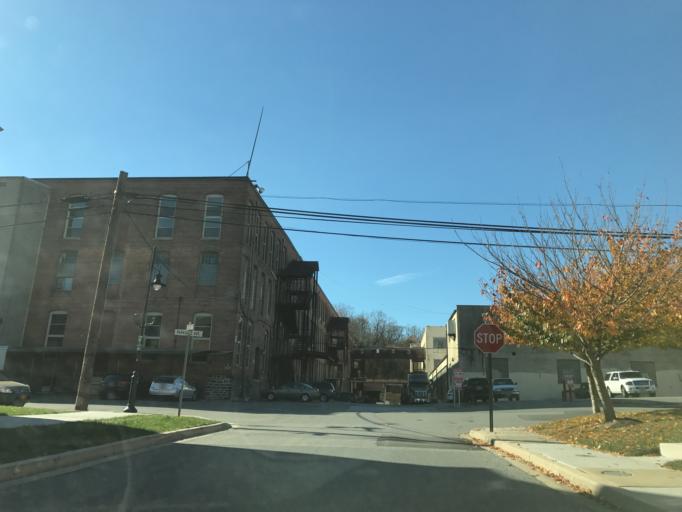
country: US
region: Maryland
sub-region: City of Baltimore
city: Baltimore
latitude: 39.3311
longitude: -76.6479
